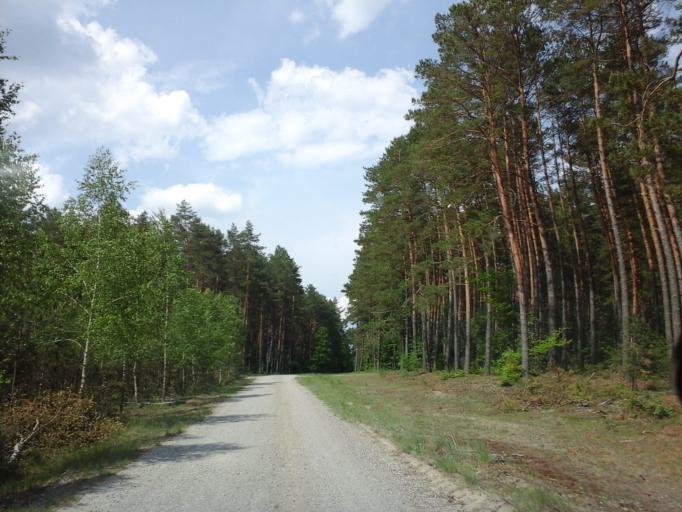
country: PL
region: West Pomeranian Voivodeship
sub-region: Powiat choszczenski
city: Drawno
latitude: 53.2039
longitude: 15.7168
